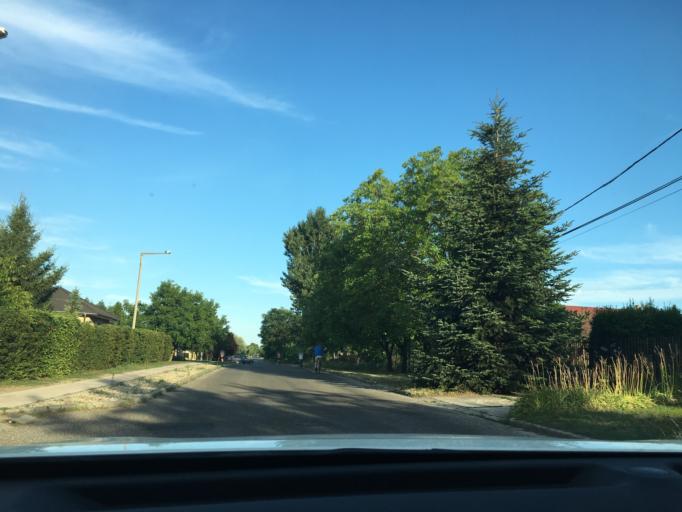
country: HU
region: Budapest
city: Budapest XVII. keruelet
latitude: 47.4736
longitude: 19.2644
